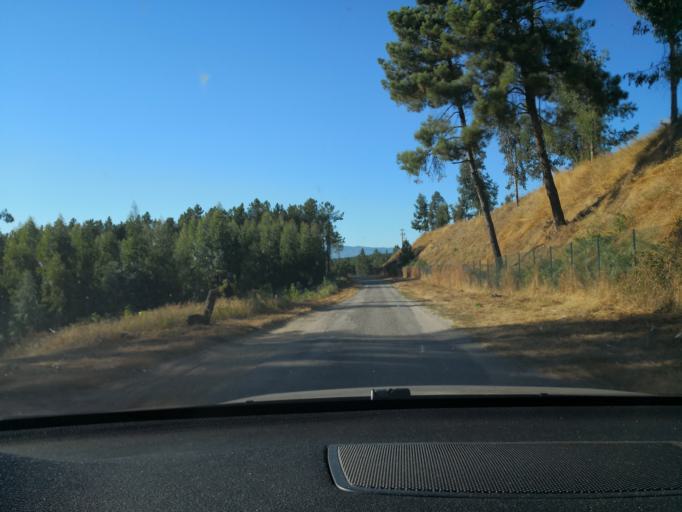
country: PT
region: Vila Real
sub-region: Sabrosa
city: Vilela
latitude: 41.2470
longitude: -7.6271
